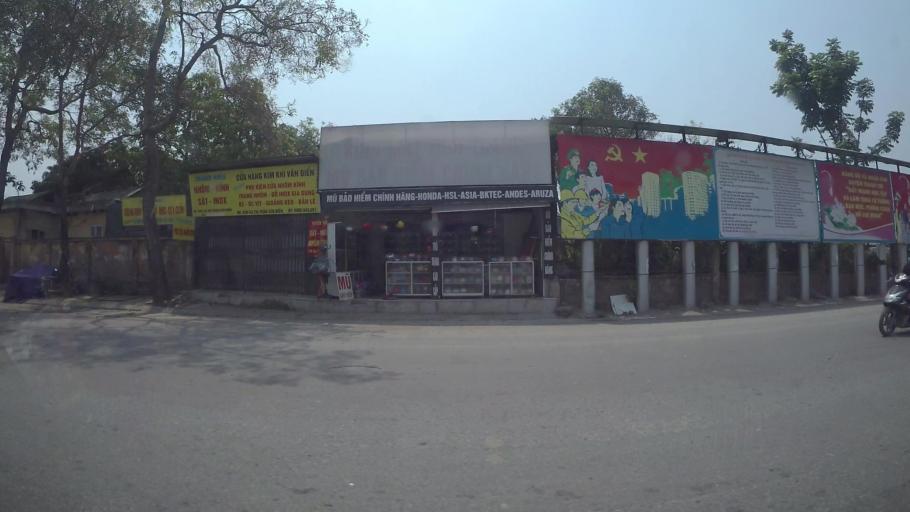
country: VN
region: Ha Noi
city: Van Dien
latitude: 20.9459
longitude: 105.8445
